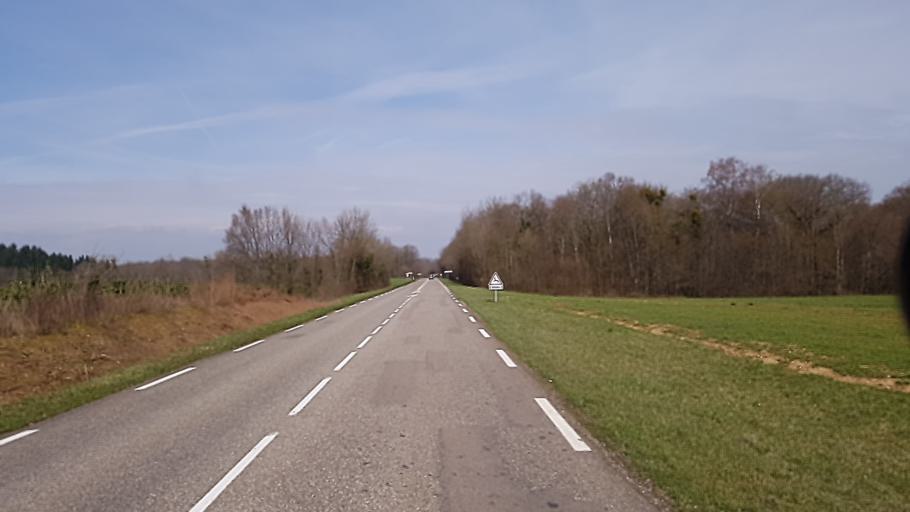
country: FR
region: Franche-Comte
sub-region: Departement du Jura
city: Mont-sous-Vaudrey
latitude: 46.9368
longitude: 5.6064
